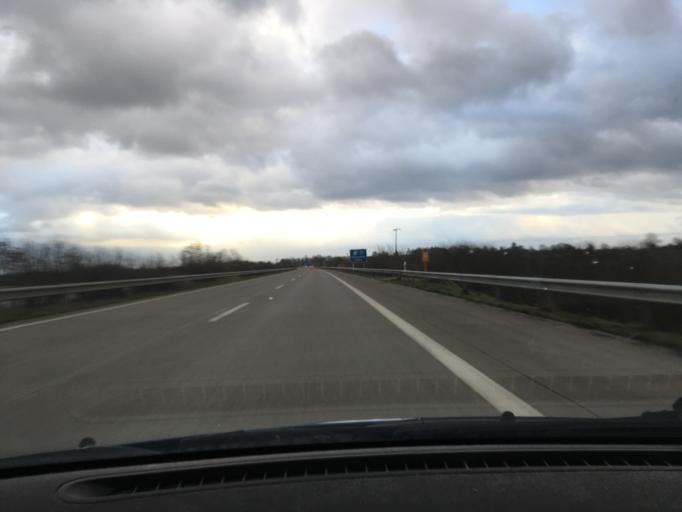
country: DE
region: Schleswig-Holstein
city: Rethwisch
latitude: 53.8512
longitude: 9.5847
